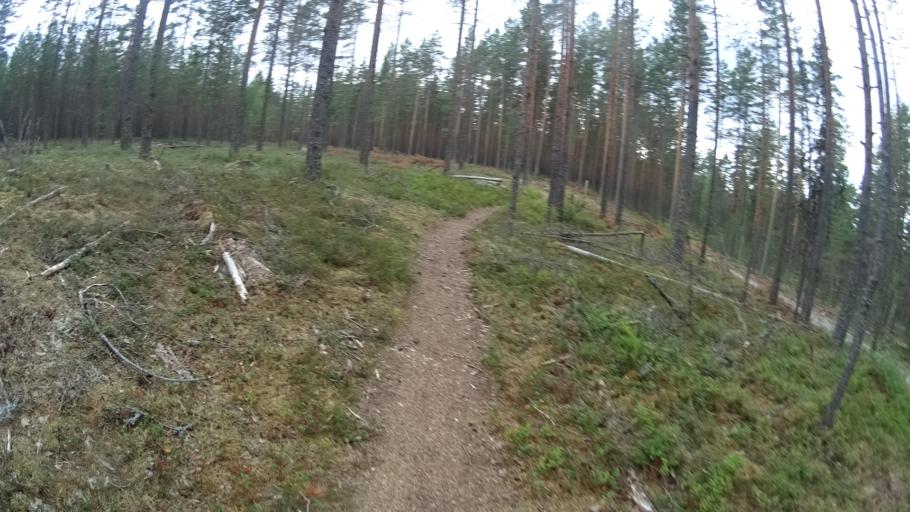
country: FI
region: Satakunta
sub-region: Pohjois-Satakunta
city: Jaemijaervi
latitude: 61.7700
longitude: 22.7721
